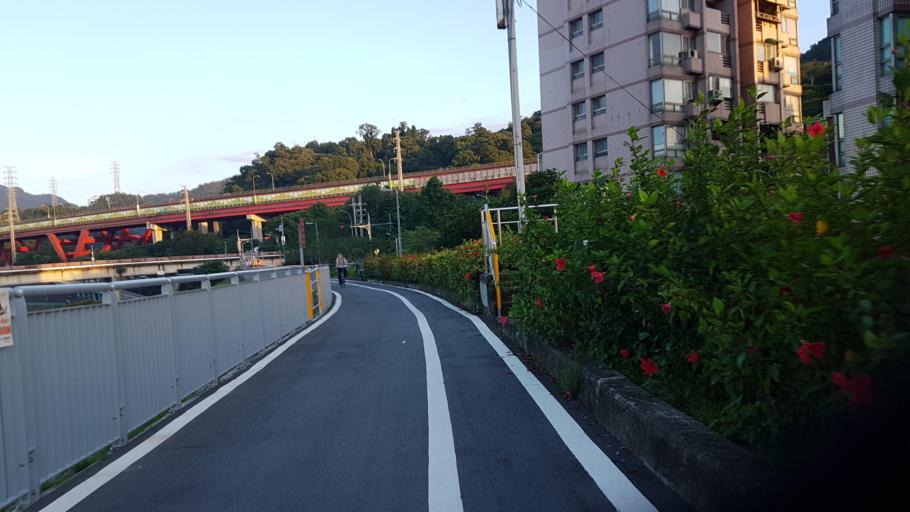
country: TW
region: Taipei
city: Taipei
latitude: 24.9765
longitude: 121.5543
